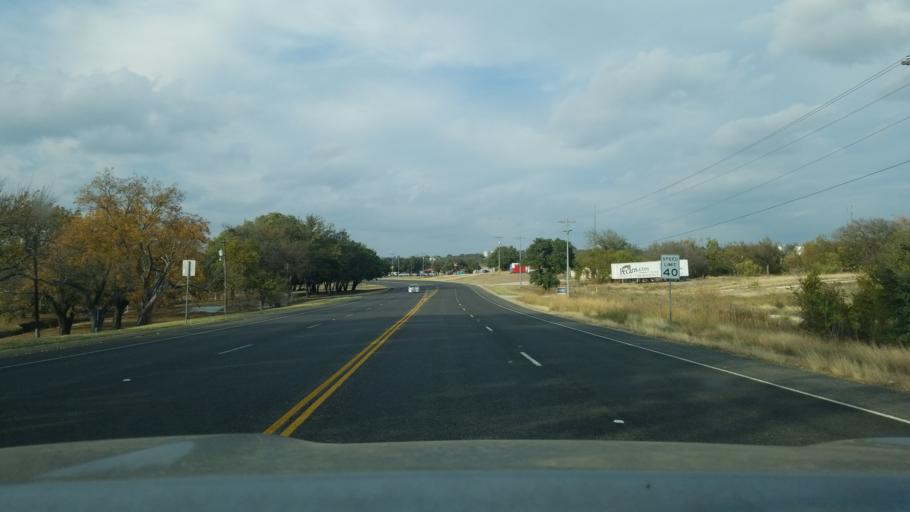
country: US
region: Texas
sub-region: Mills County
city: Goldthwaite
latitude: 31.4433
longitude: -98.5676
